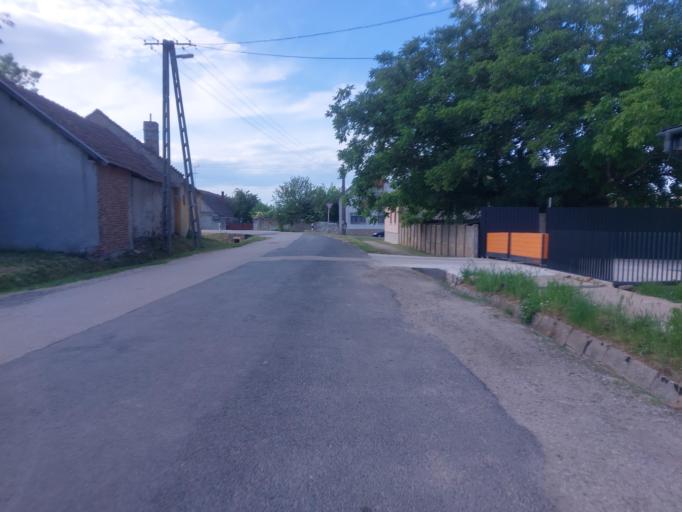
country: HU
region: Veszprem
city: Devecser
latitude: 47.1662
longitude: 17.3784
